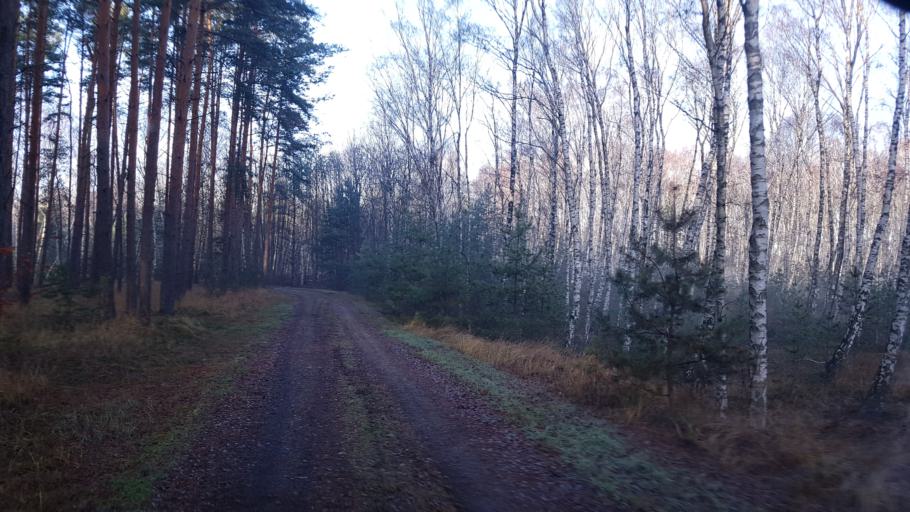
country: DE
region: Brandenburg
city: Schonborn
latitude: 51.5845
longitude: 13.4776
